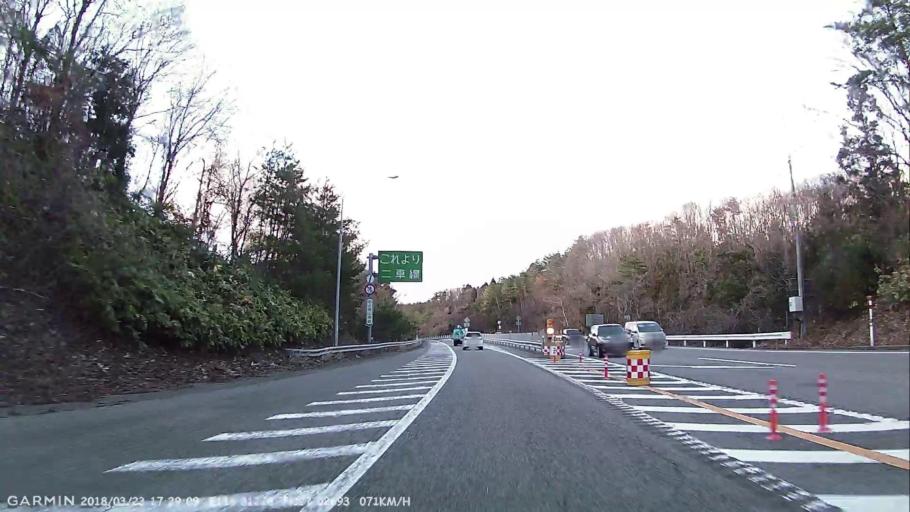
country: JP
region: Ishikawa
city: Hakui
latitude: 37.0271
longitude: 136.8124
